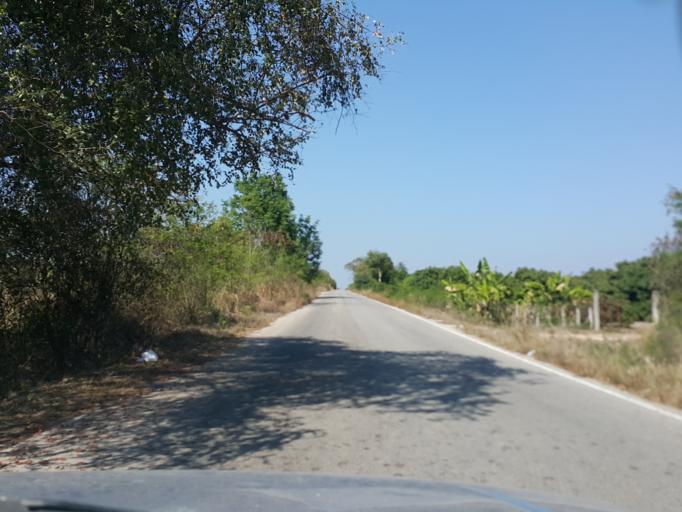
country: TH
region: Chiang Mai
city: Mae Wang
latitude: 18.5412
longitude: 98.7967
